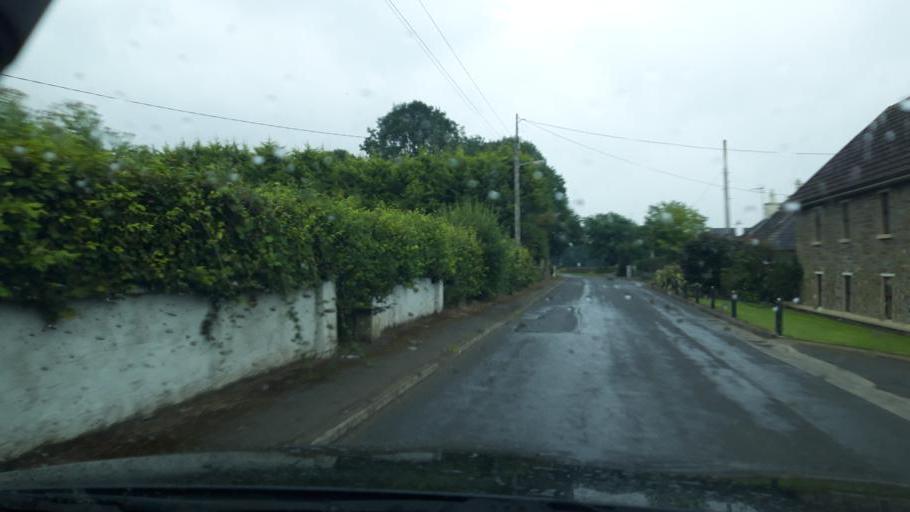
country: IE
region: Leinster
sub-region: Kilkenny
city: Callan
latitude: 52.6616
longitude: -7.4378
